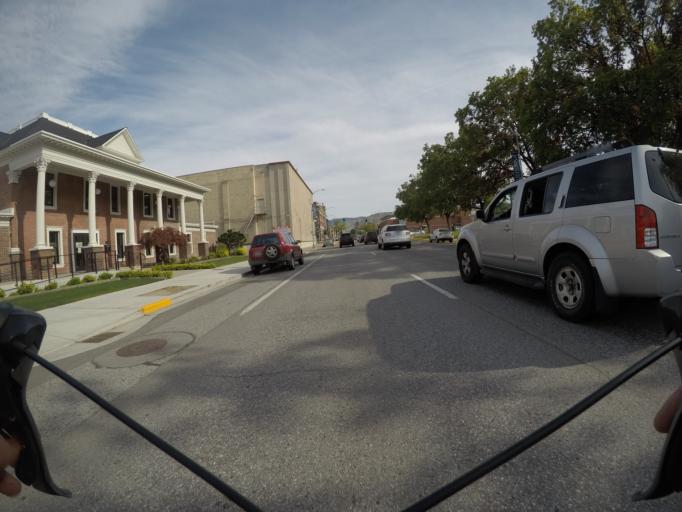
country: US
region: Washington
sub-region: Chelan County
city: Wenatchee
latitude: 47.4233
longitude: -120.3134
